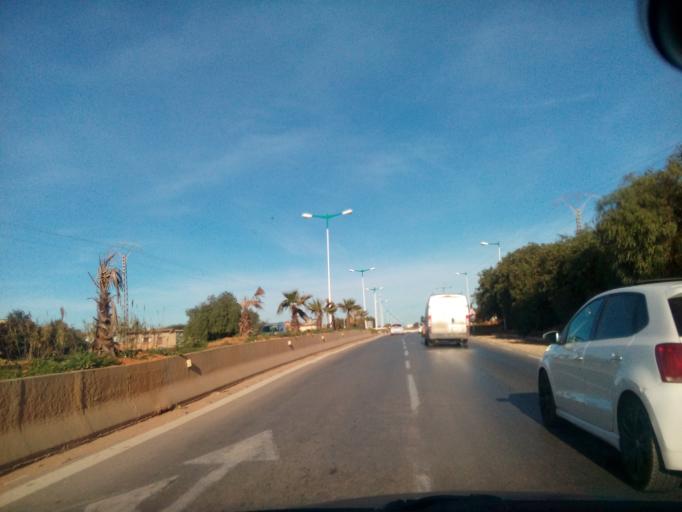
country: DZ
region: Mostaganem
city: Mostaganem
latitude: 35.8688
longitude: 0.1511
